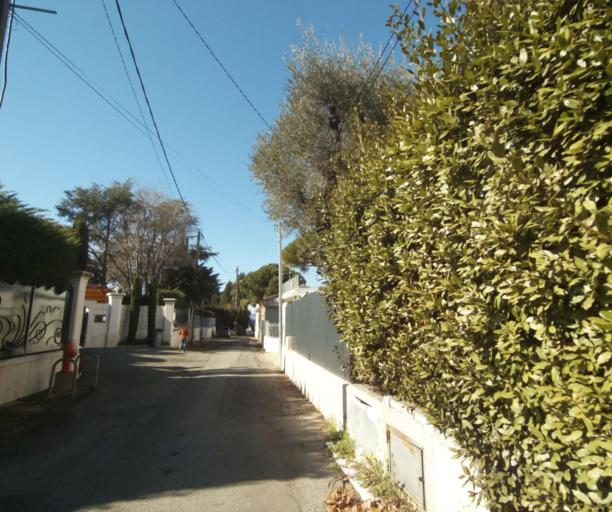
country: FR
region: Provence-Alpes-Cote d'Azur
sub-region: Departement des Alpes-Maritimes
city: Antibes
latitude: 43.5521
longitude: 7.1234
